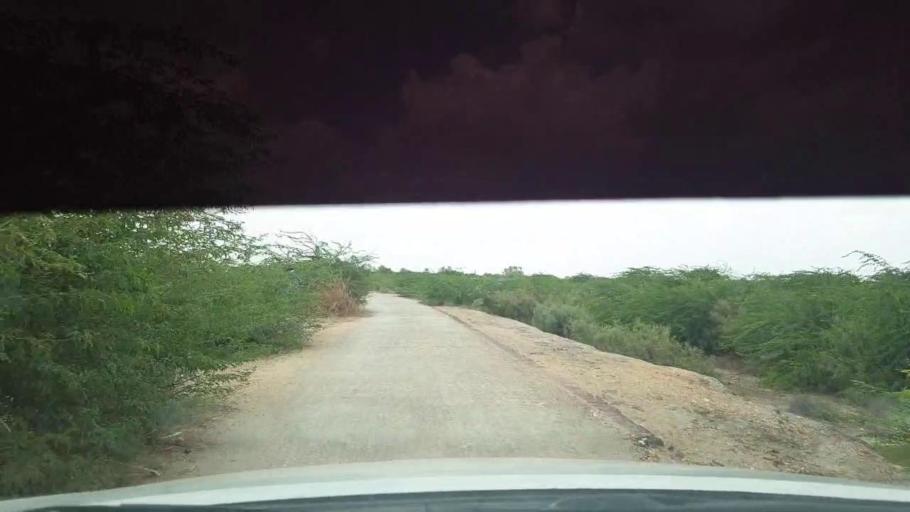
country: PK
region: Sindh
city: Kadhan
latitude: 24.4645
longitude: 69.0403
